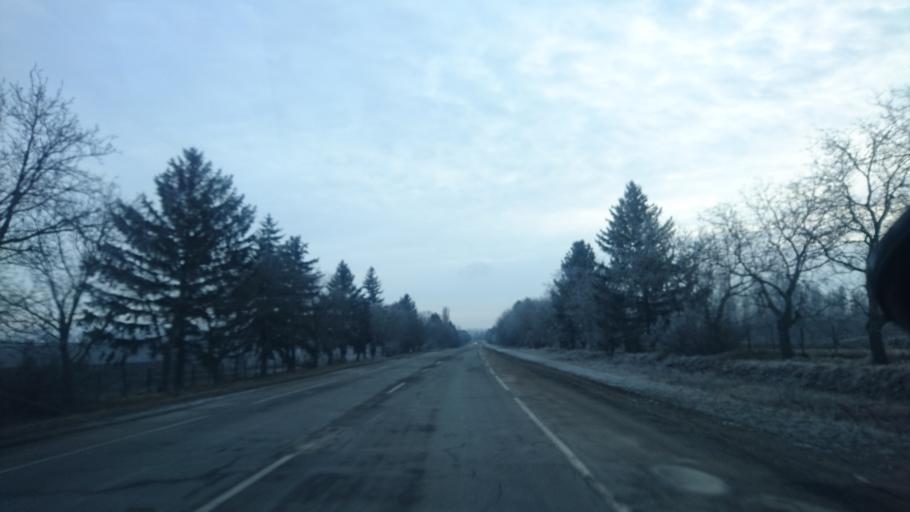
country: MD
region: Briceni
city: Briceni
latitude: 48.3065
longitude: 27.1237
